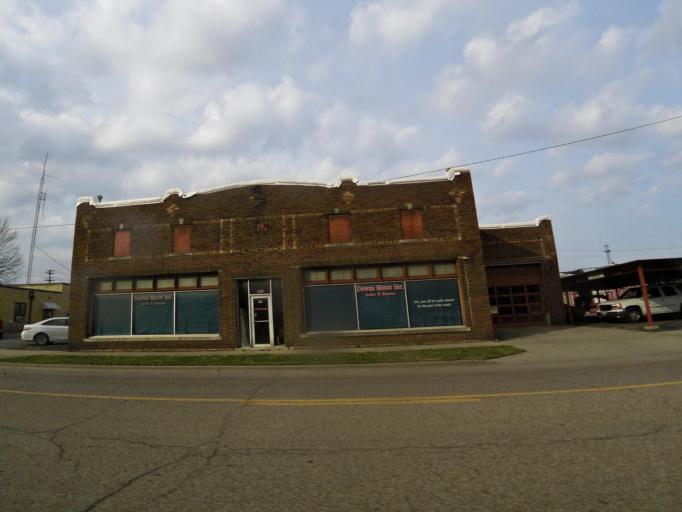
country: US
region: Illinois
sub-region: Christian County
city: Pana
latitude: 39.3883
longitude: -89.0805
